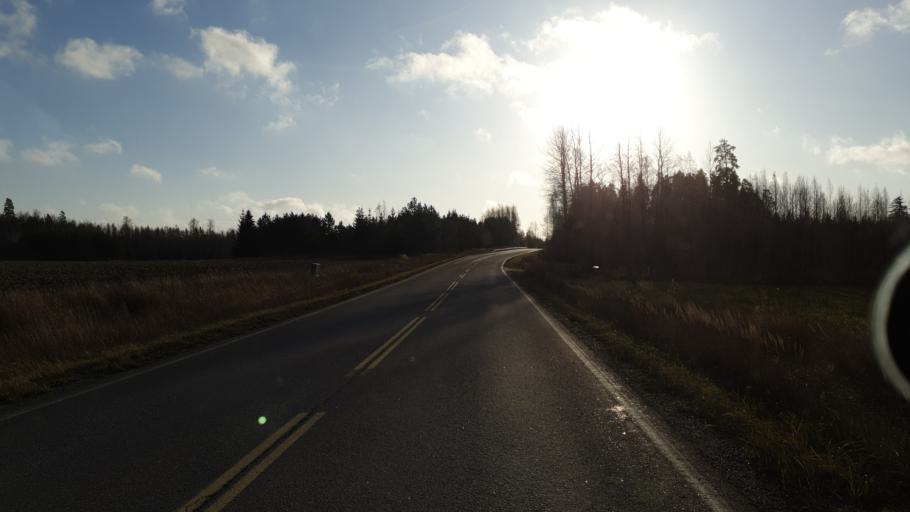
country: FI
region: Uusimaa
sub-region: Helsinki
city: Siuntio
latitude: 60.2245
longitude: 24.1680
